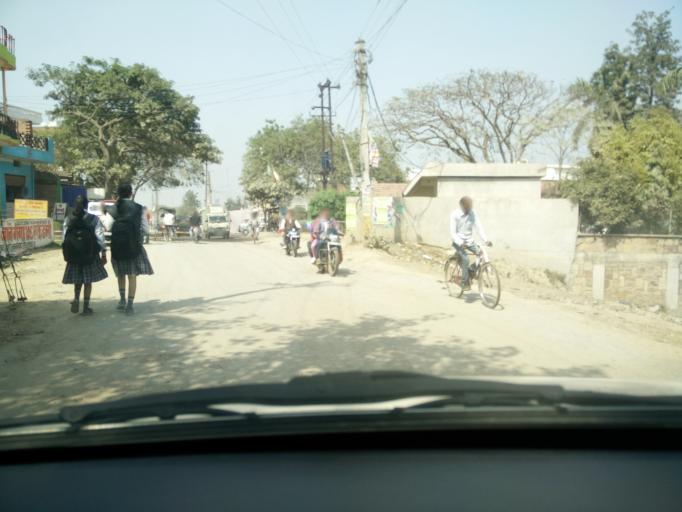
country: IN
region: Uttar Pradesh
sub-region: Varanasi
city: Ramnagar
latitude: 25.2675
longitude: 83.0161
